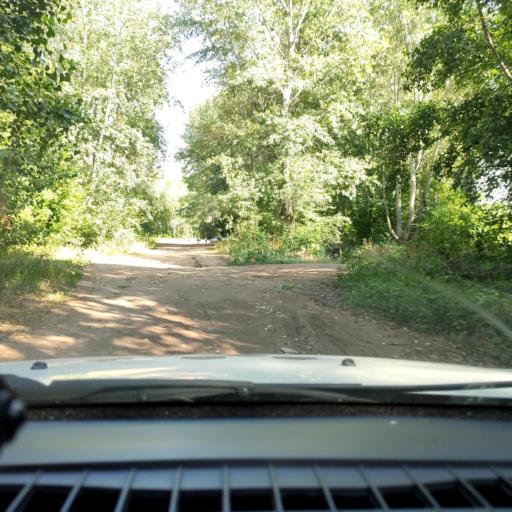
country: RU
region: Samara
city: Smyshlyayevka
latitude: 53.2051
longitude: 50.3297
